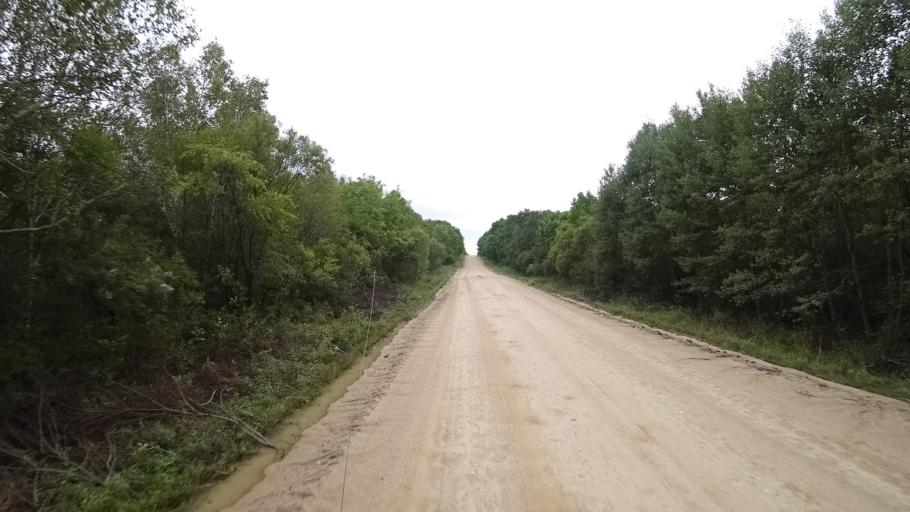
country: RU
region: Primorskiy
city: Monastyrishche
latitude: 44.1119
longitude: 132.6216
